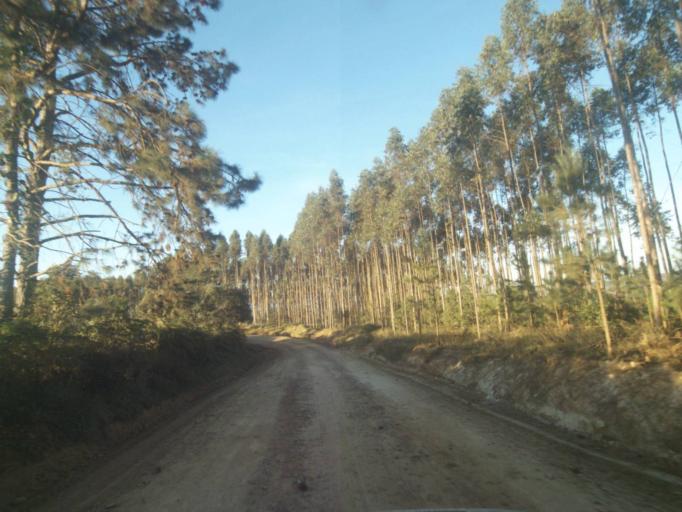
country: BR
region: Parana
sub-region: Tibagi
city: Tibagi
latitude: -24.5468
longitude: -50.5326
